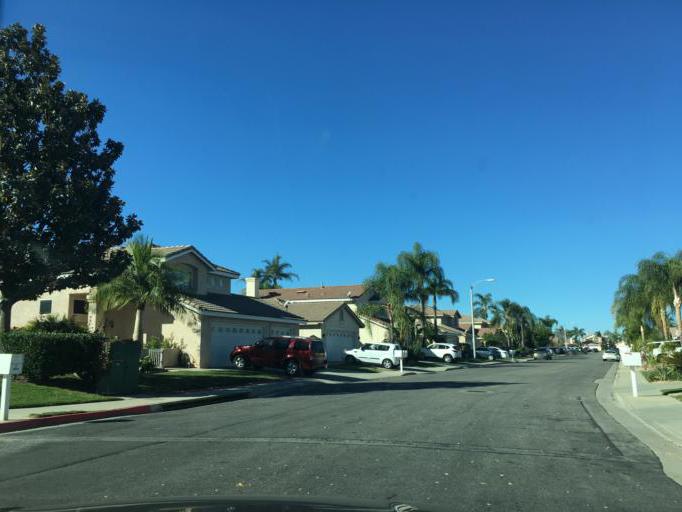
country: US
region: California
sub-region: Riverside County
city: Corona
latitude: 33.8492
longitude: -117.5529
